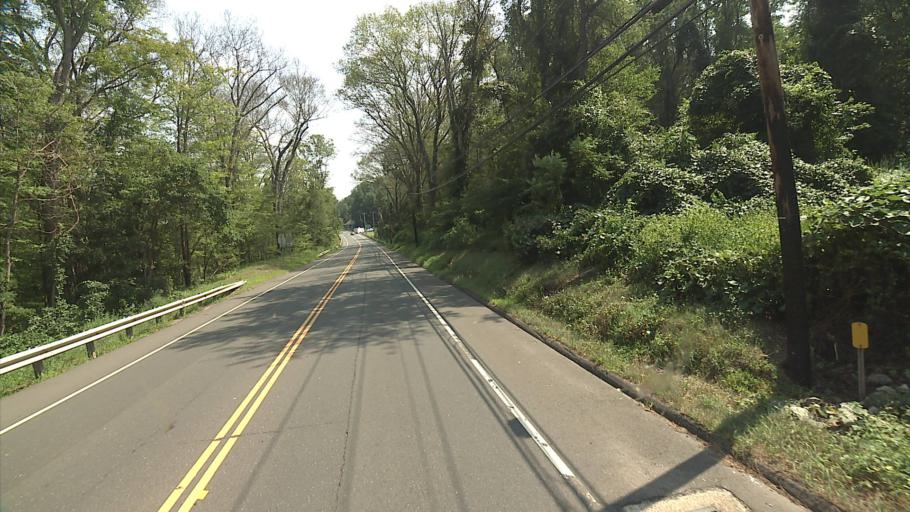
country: US
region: Connecticut
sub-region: Middlesex County
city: East Haddam
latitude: 41.4455
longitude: -72.4729
